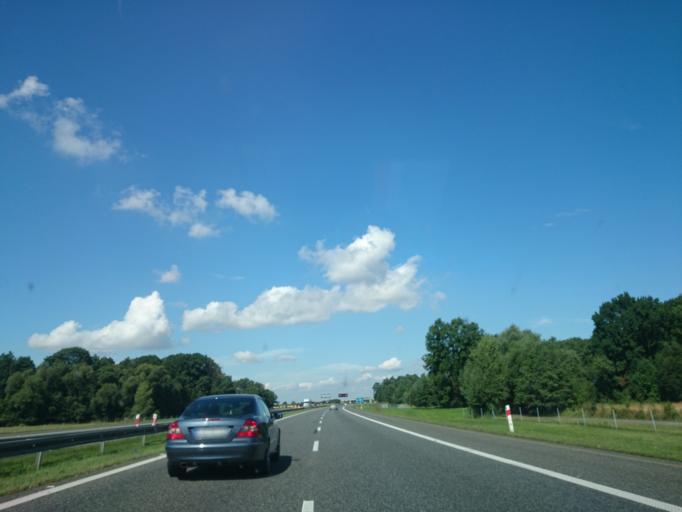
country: PL
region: Opole Voivodeship
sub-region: Powiat brzeski
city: Grodkow
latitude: 50.7740
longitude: 17.3675
